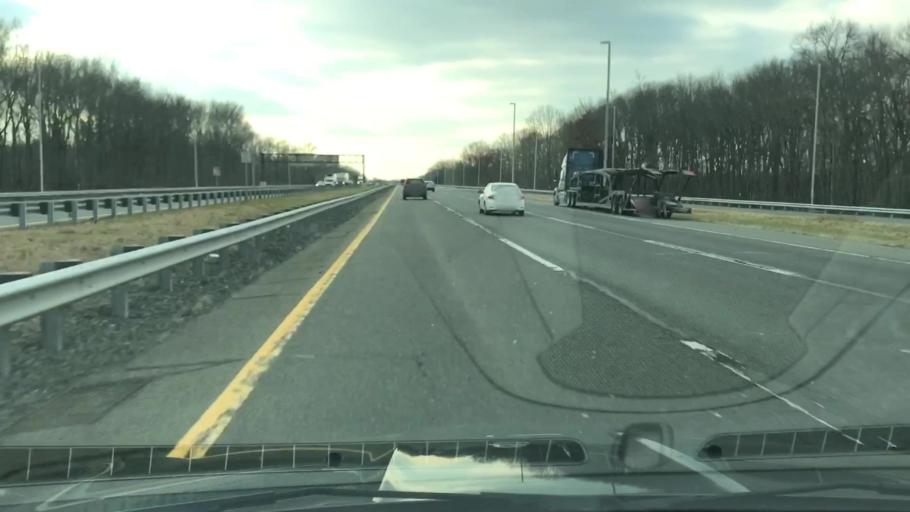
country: US
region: New Jersey
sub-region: Burlington County
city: Roebling
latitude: 40.0968
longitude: -74.7376
